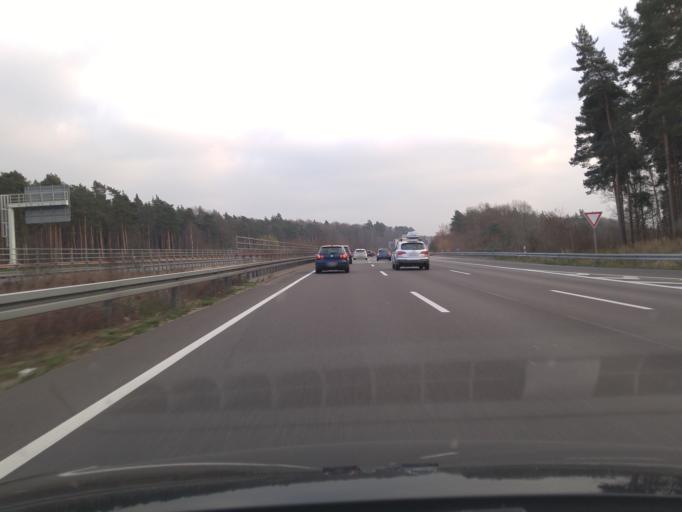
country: DE
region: Lower Saxony
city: Mariental
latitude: 52.2628
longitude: 10.9854
